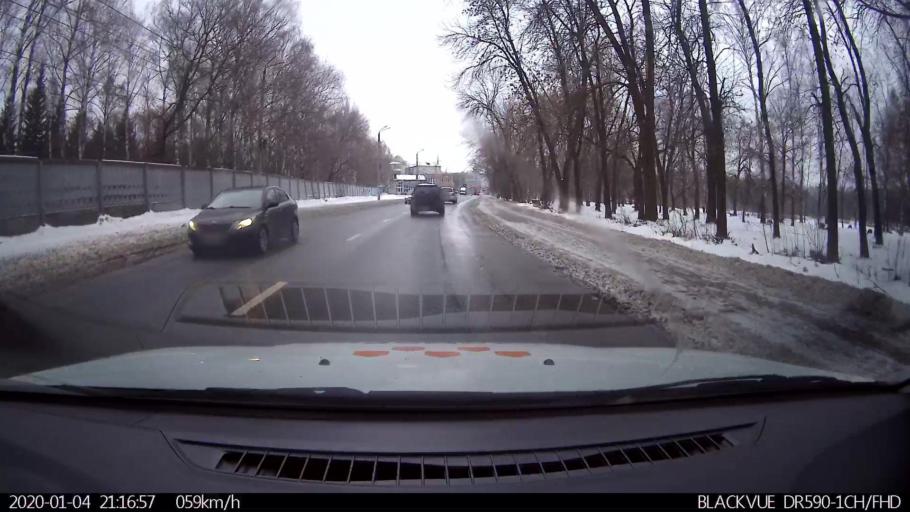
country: RU
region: Nizjnij Novgorod
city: Gorbatovka
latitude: 56.2371
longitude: 43.8511
